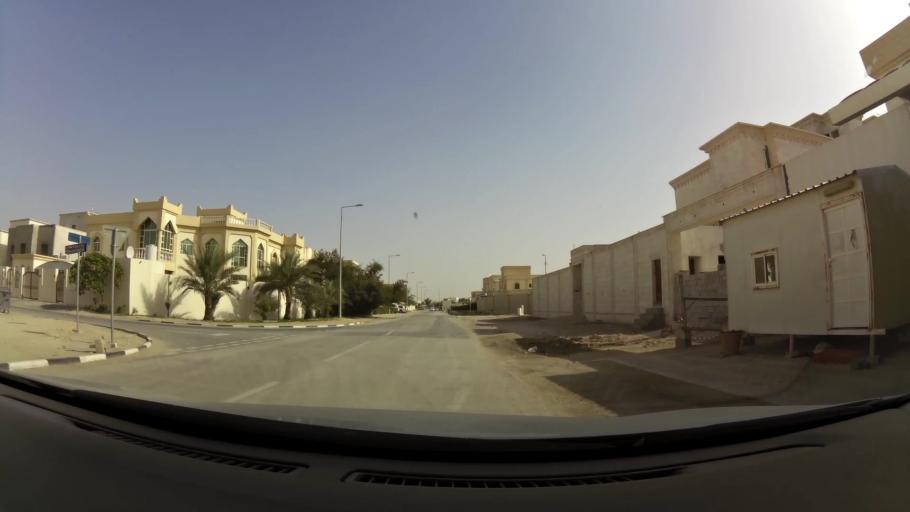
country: QA
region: Baladiyat ar Rayyan
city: Ar Rayyan
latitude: 25.3423
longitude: 51.4284
